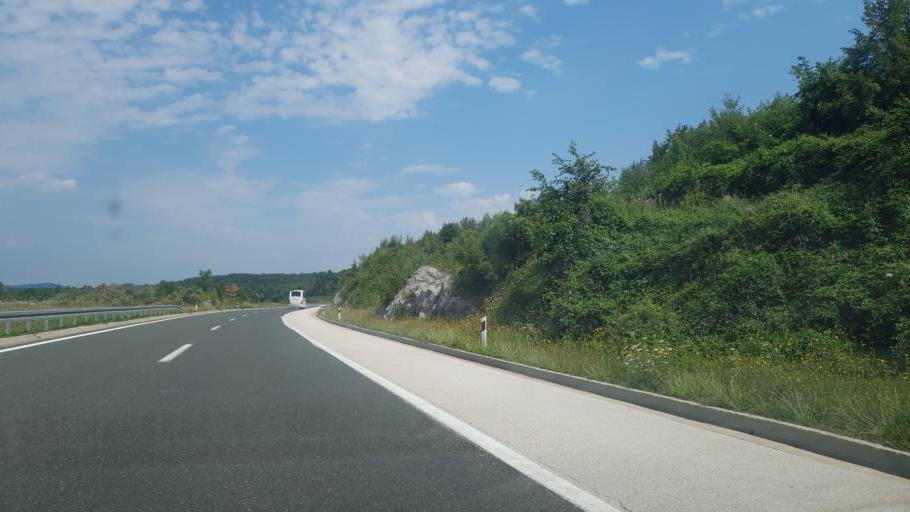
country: HR
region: Primorsko-Goranska
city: Matulji
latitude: 45.4222
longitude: 14.2996
